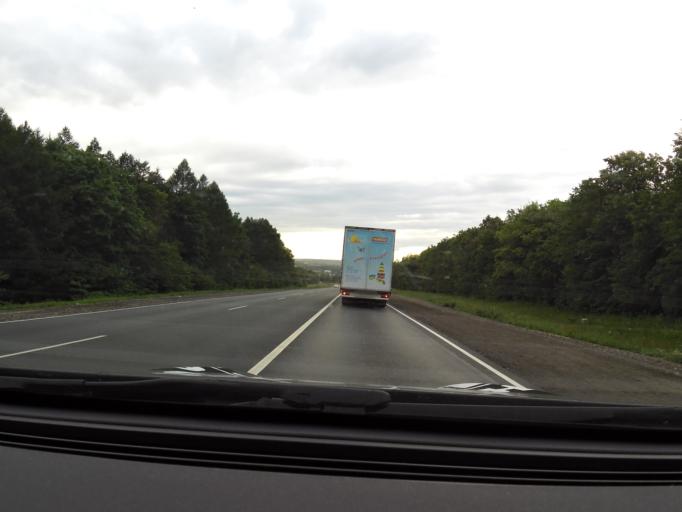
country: RU
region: Chuvashia
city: Tsivil'sk
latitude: 55.8422
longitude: 47.5309
